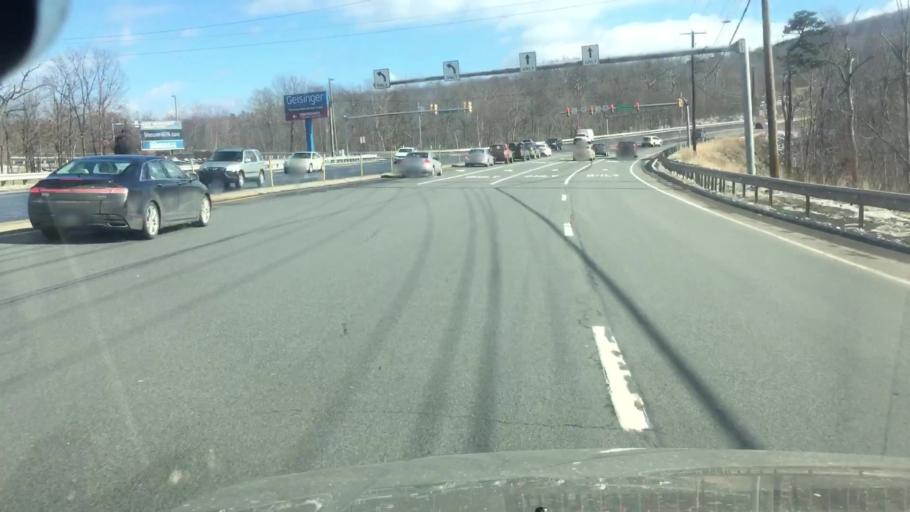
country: US
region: Pennsylvania
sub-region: Luzerne County
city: Hudson
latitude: 41.2489
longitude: -75.8105
